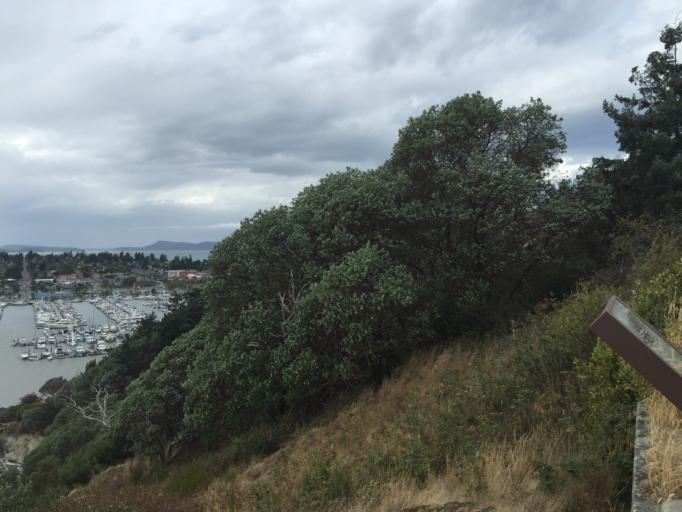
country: US
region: Washington
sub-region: Skagit County
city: Anacortes
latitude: 48.5133
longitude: -122.5992
